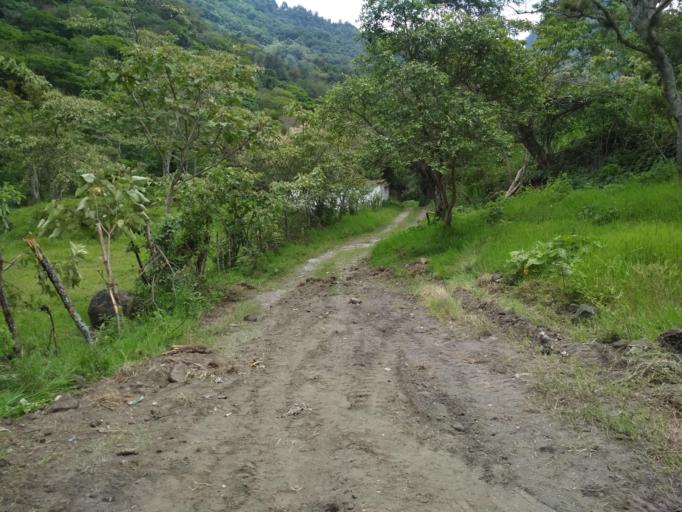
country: MX
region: Veracruz
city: Jilotepec
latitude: 19.6177
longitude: -96.9321
